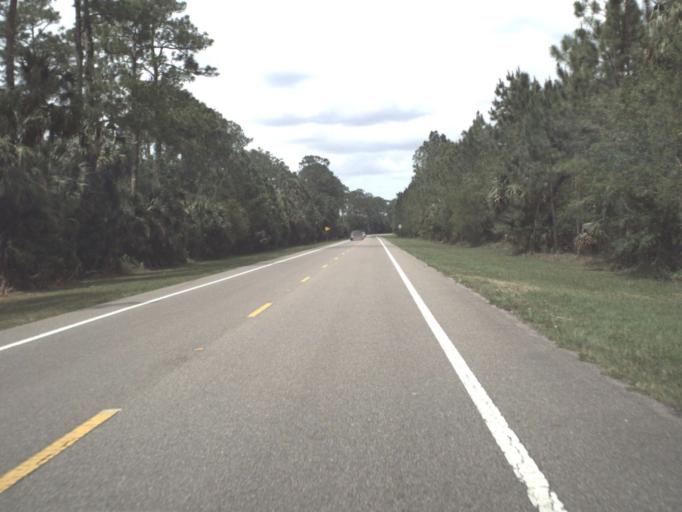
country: US
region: Florida
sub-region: Flagler County
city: Bunnell
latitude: 29.4094
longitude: -81.3054
